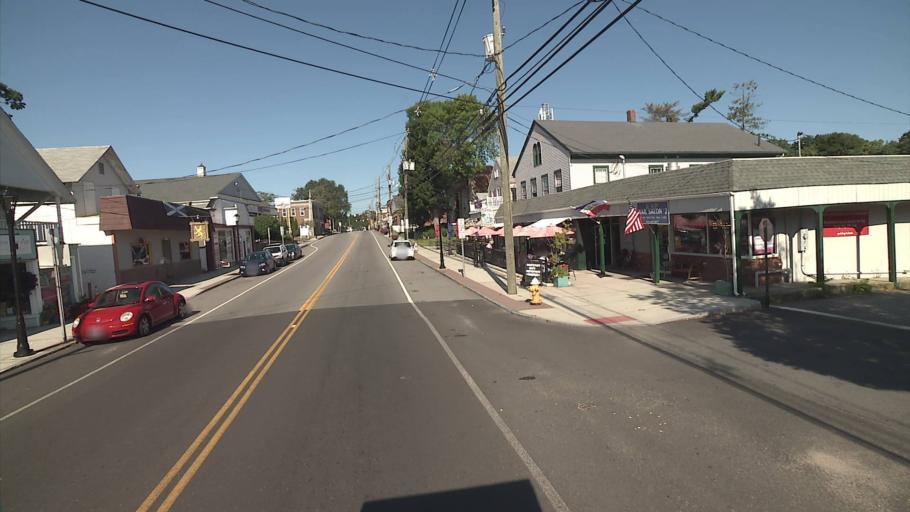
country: US
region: Connecticut
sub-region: Middlesex County
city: Clinton
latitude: 41.2785
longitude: -72.5252
